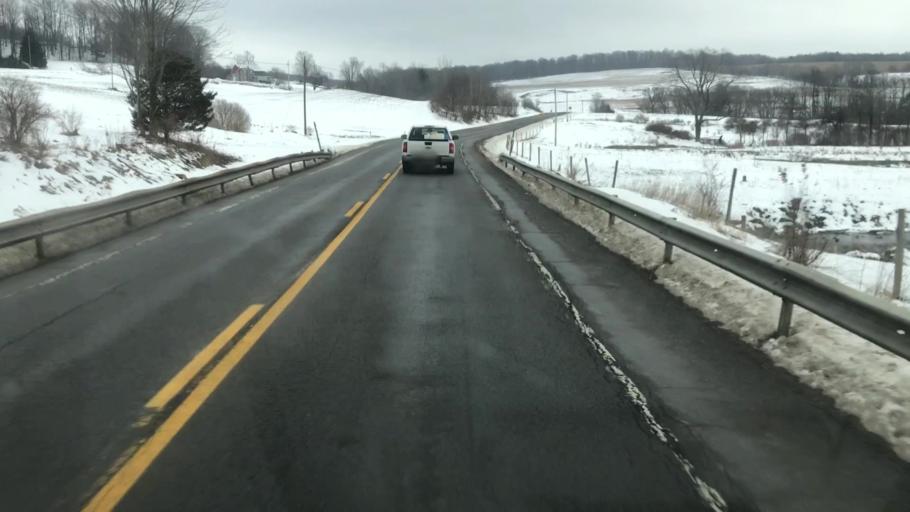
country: US
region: New York
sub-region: Cortland County
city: Cortland West
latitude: 42.6751
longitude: -76.2819
